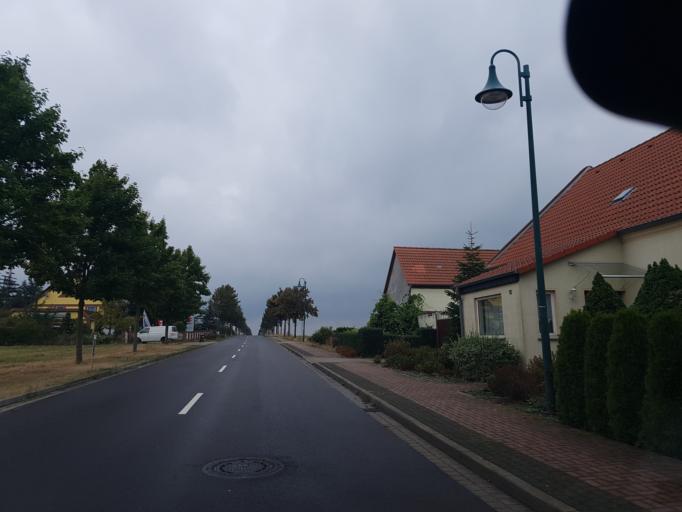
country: DE
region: Saxony-Anhalt
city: Tucheim
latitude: 52.2930
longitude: 12.1744
